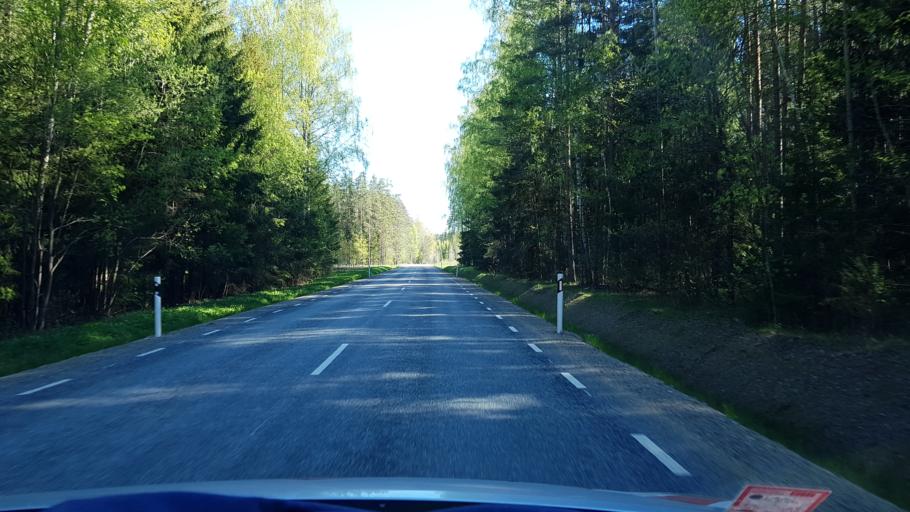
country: EE
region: Polvamaa
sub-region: Polva linn
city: Polva
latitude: 58.1061
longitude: 27.1081
